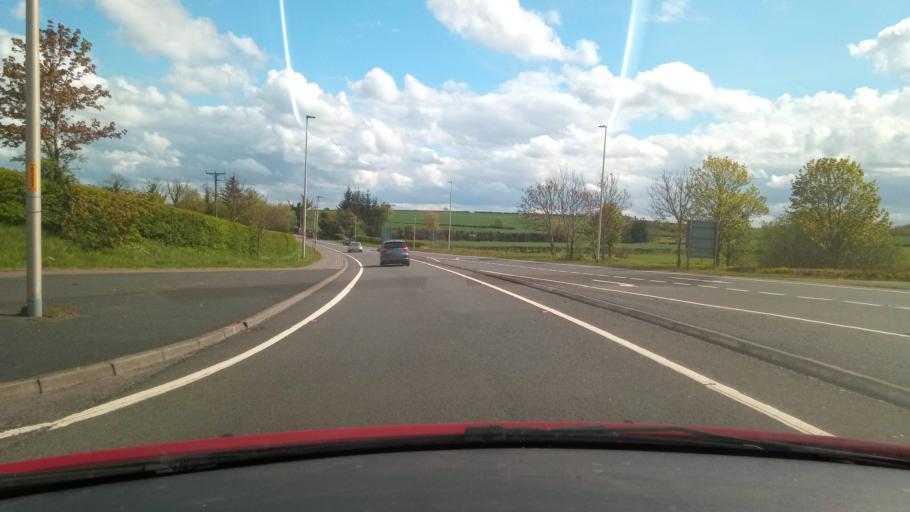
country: GB
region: Scotland
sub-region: The Scottish Borders
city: Saint Boswells
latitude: 55.5741
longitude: -2.6627
